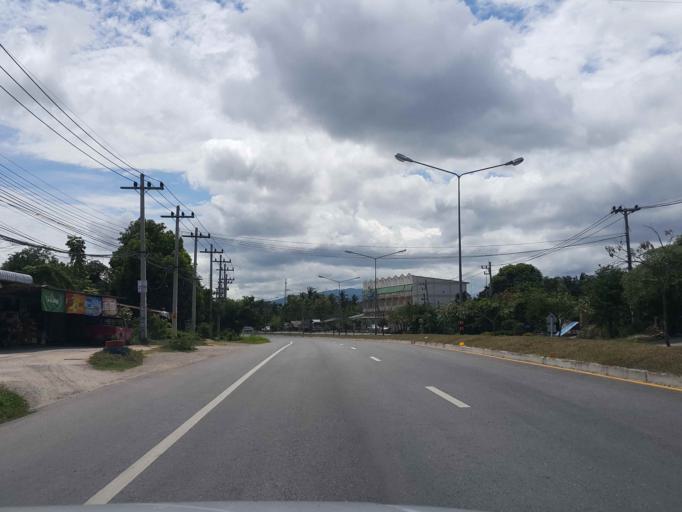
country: TH
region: Tak
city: Tak
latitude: 16.8877
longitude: 99.1677
